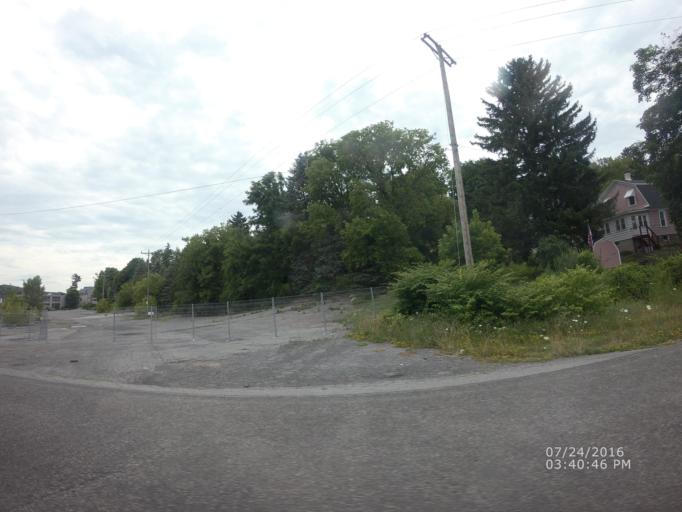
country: US
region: New York
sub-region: Onondaga County
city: Camillus
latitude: 43.0412
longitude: -76.3076
